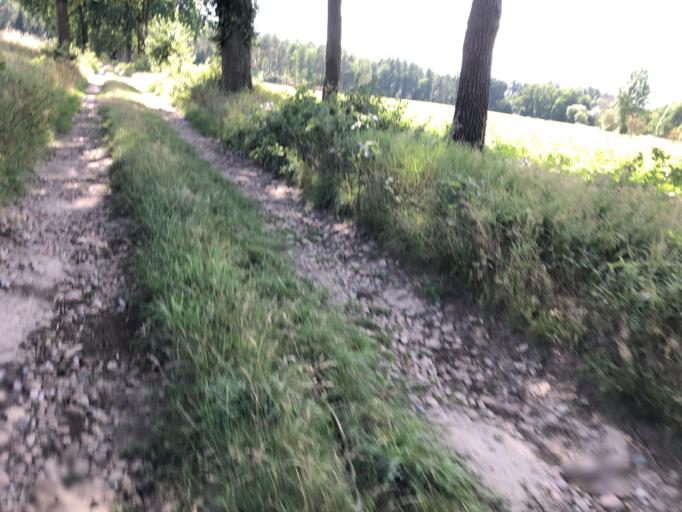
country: DE
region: Lower Saxony
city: Thomasburg
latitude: 53.2072
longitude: 10.6988
